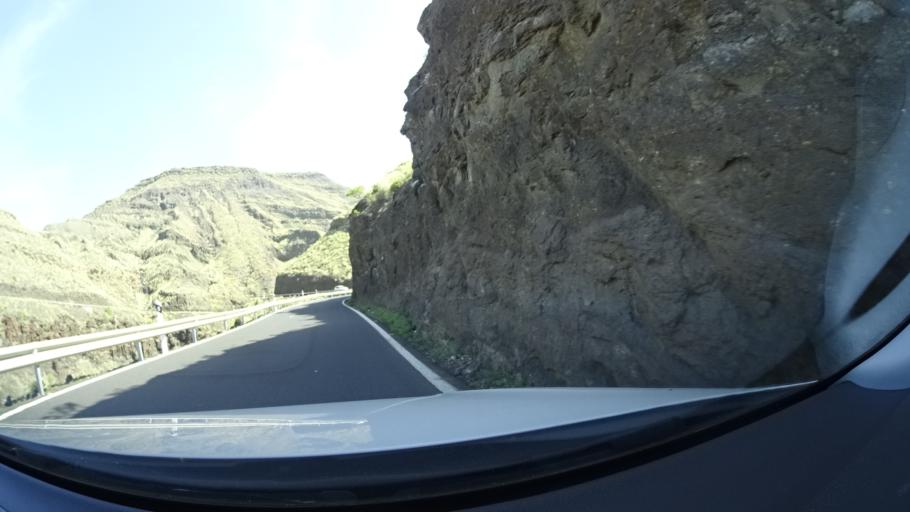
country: ES
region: Canary Islands
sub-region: Provincia de Las Palmas
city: Agaete
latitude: 28.0836
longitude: -15.7050
